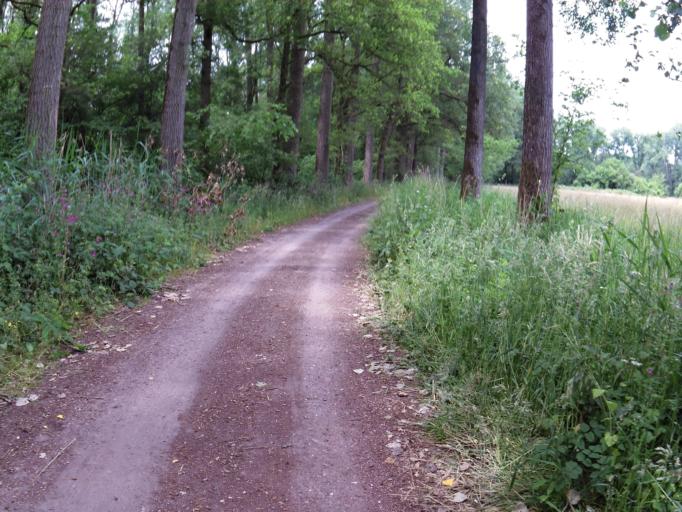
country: NL
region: North Brabant
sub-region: Gemeente Oirschot
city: Oirschot
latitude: 51.5361
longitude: 5.3438
